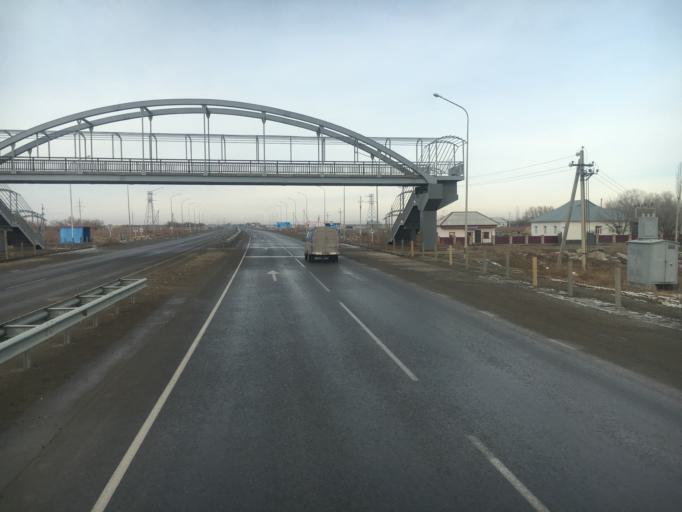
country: KZ
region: Qyzylorda
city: Shieli
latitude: 44.1378
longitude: 66.9684
